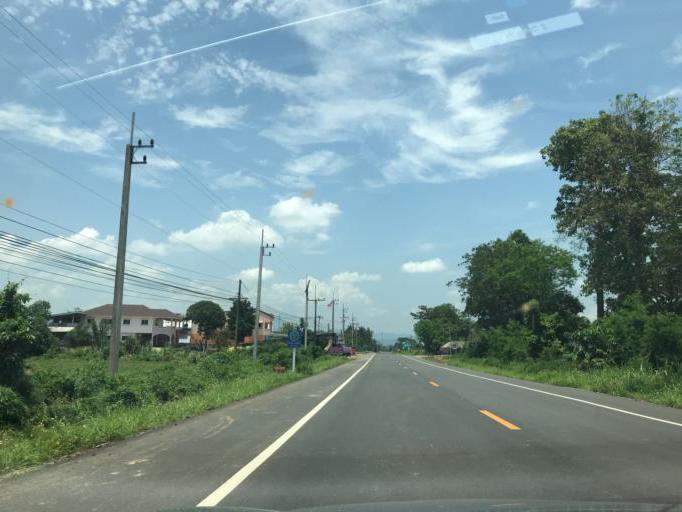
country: TH
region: Phayao
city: Phu Sang
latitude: 19.5852
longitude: 100.3086
